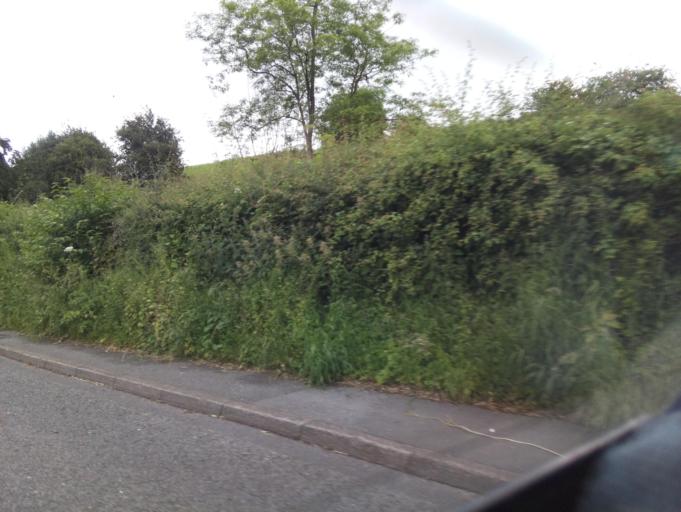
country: GB
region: England
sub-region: Derbyshire
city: Ashbourne
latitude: 53.0130
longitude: -1.7279
